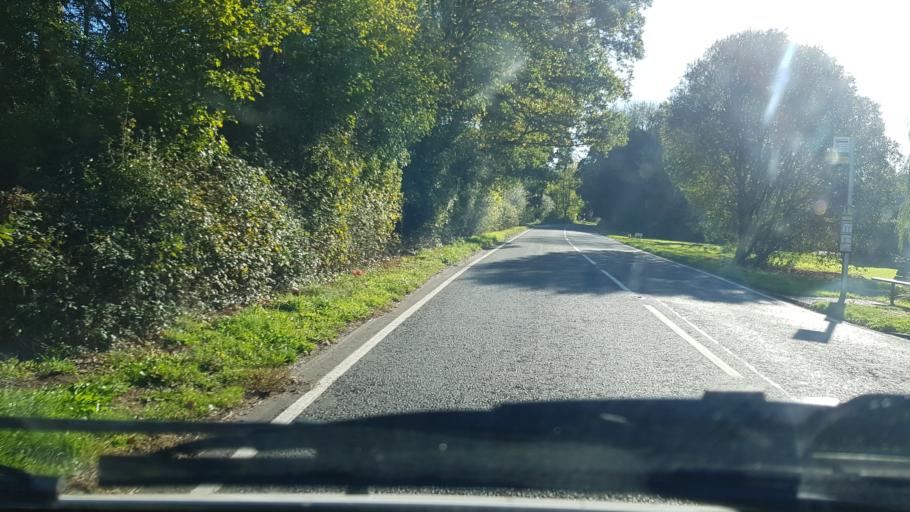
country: GB
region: England
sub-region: Surrey
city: Cranleigh
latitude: 51.1740
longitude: -0.5152
